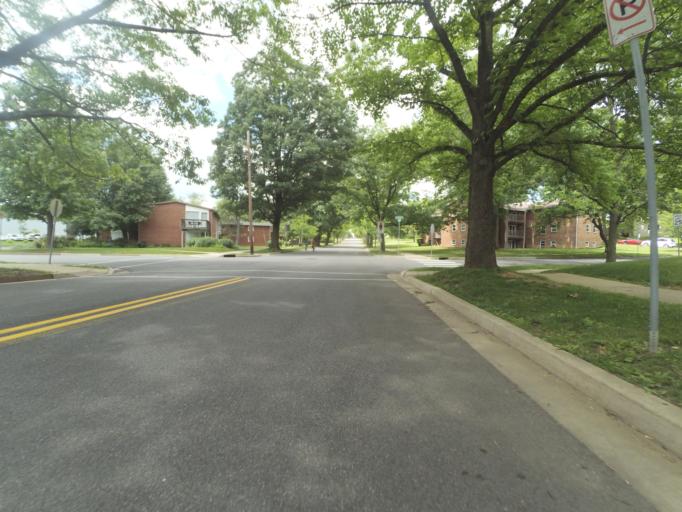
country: US
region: Pennsylvania
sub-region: Centre County
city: State College
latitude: 40.7812
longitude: -77.8718
